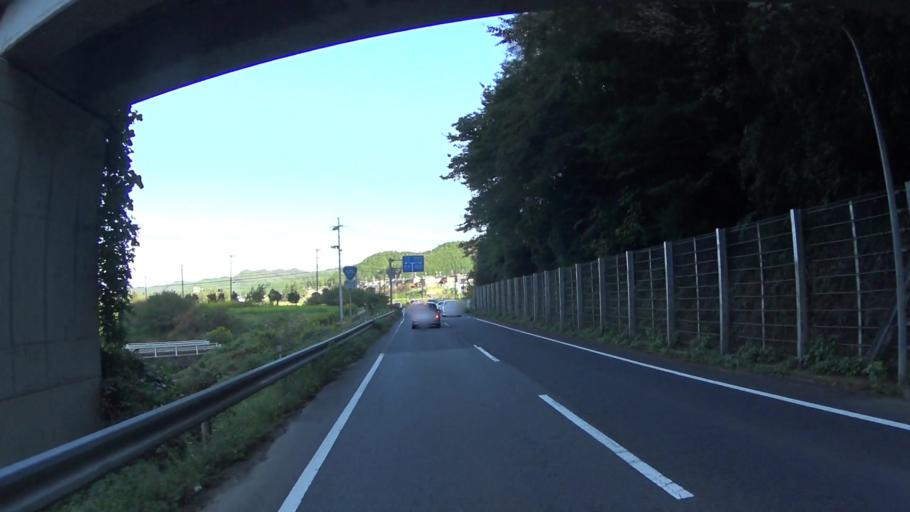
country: JP
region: Kyoto
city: Fukuchiyama
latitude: 35.3634
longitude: 135.1133
